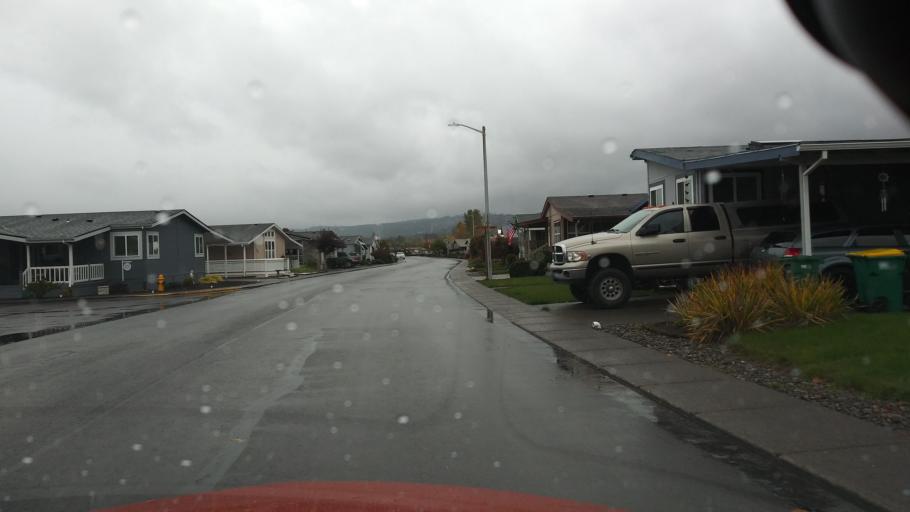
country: US
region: Oregon
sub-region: Washington County
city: Cornelius
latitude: 45.5134
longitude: -123.0741
